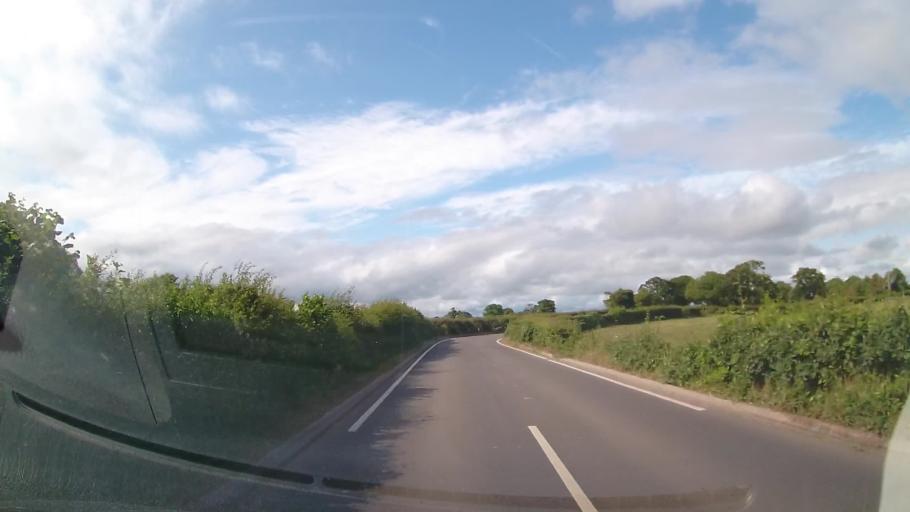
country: GB
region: England
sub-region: Shropshire
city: Petton
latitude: 52.8479
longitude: -2.8034
